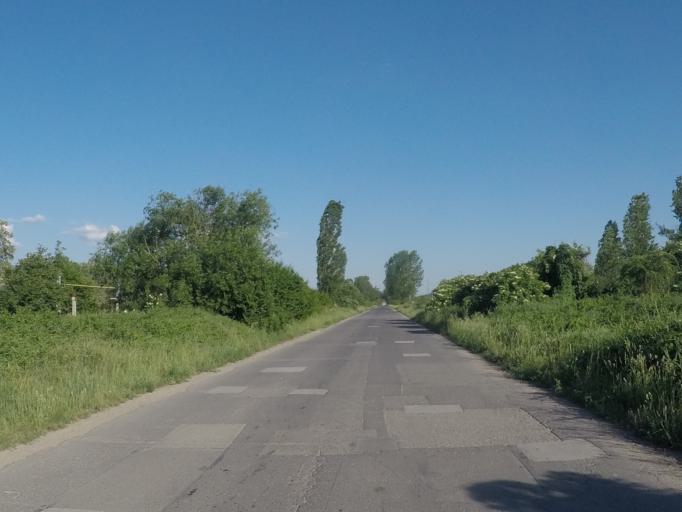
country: HU
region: Borsod-Abauj-Zemplen
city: Mucsony
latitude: 48.2480
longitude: 20.6639
